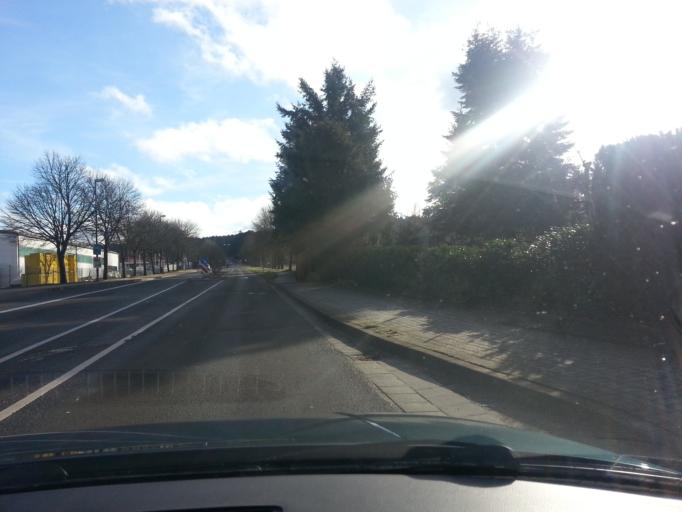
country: DE
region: Rheinland-Pfalz
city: Rodenbach
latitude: 49.4722
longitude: 7.6649
